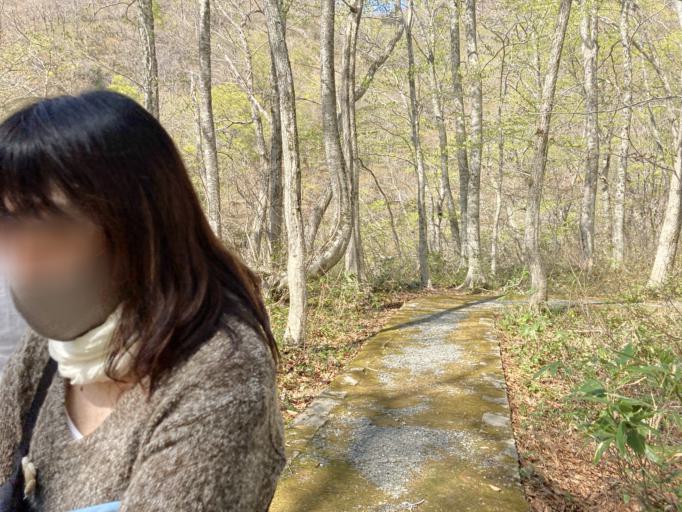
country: JP
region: Iwate
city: Ichinoseki
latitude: 39.0051
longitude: 140.8492
